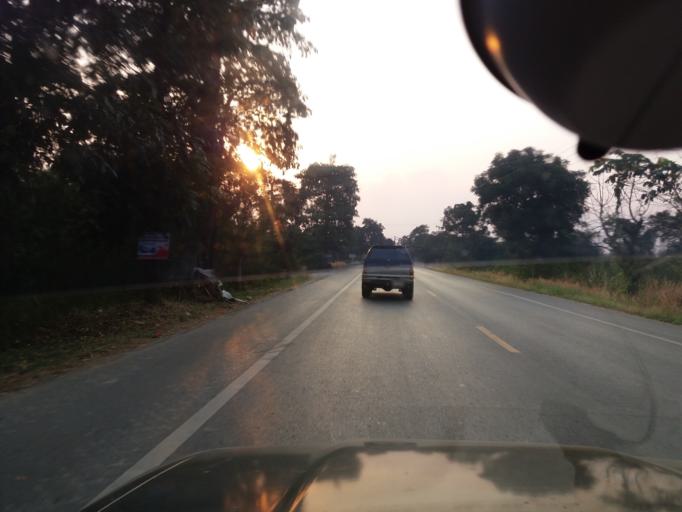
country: TH
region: Sing Buri
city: Bang Racham
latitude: 14.8819
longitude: 100.3579
